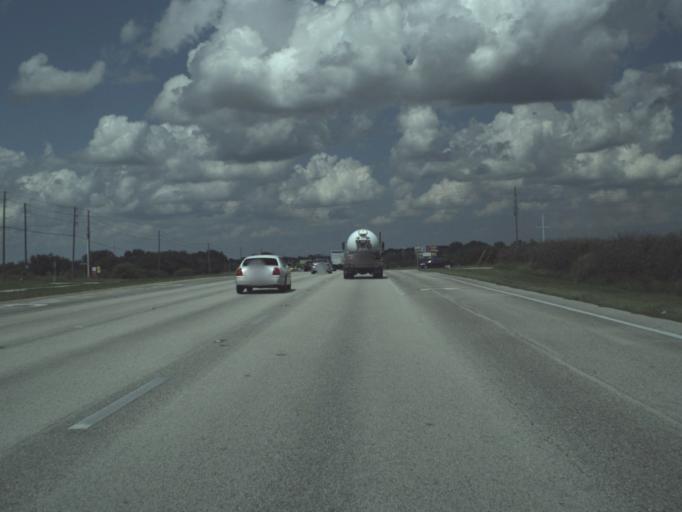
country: US
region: Florida
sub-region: Polk County
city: Davenport
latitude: 28.1855
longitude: -81.6397
